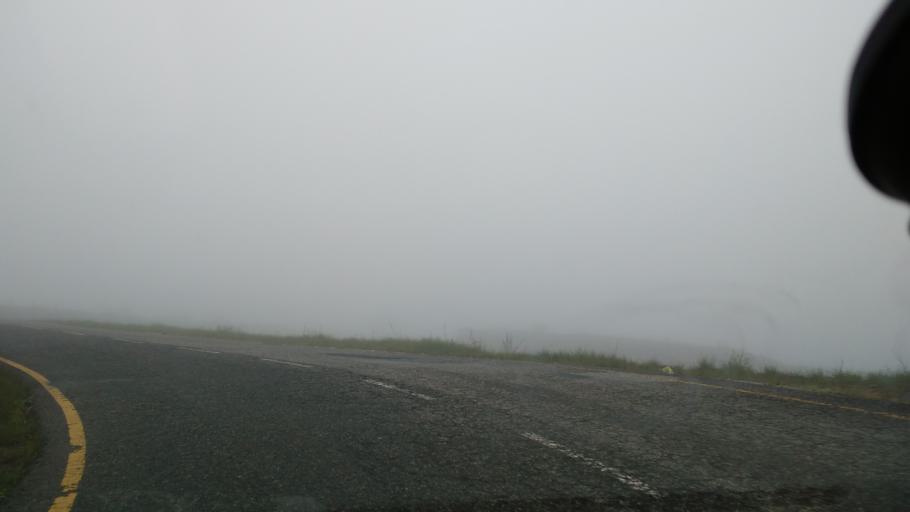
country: IN
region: Meghalaya
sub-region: East Khasi Hills
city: Cherrapunji
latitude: 25.3141
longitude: 91.7312
